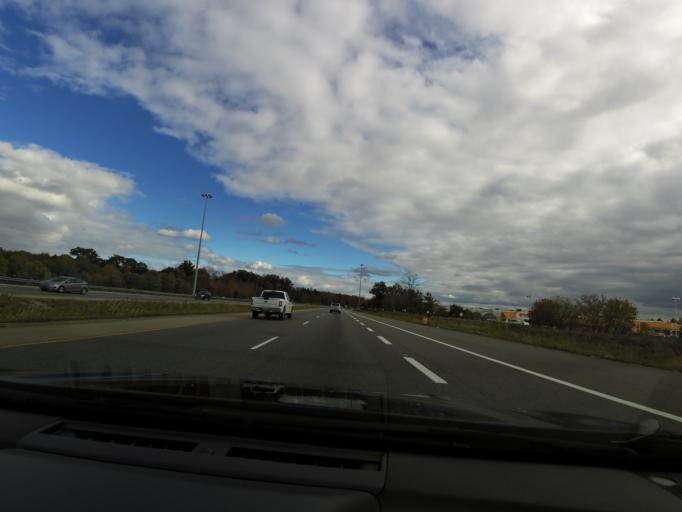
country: CA
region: Ontario
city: Cambridge
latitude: 43.4097
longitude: -80.3900
